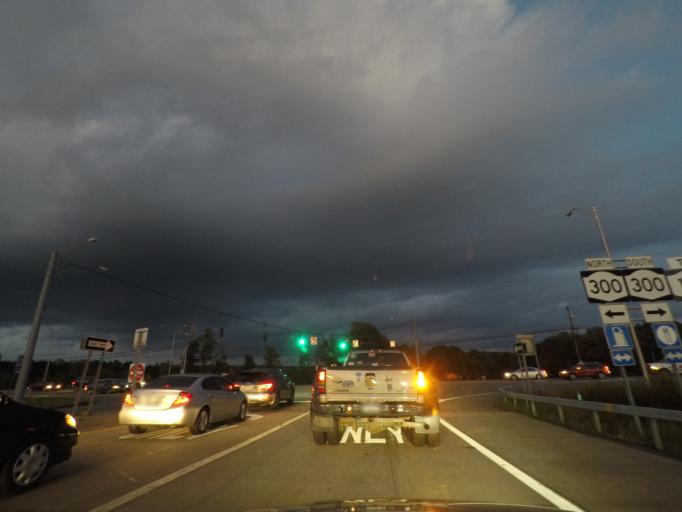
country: US
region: New York
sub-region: Orange County
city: Gardnertown
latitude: 41.5155
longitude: -74.0678
